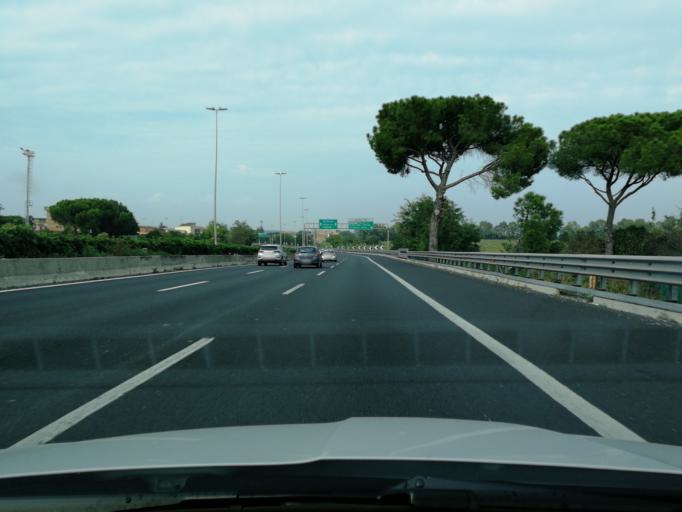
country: IT
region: Latium
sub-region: Citta metropolitana di Roma Capitale
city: Setteville
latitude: 41.9126
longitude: 12.6159
